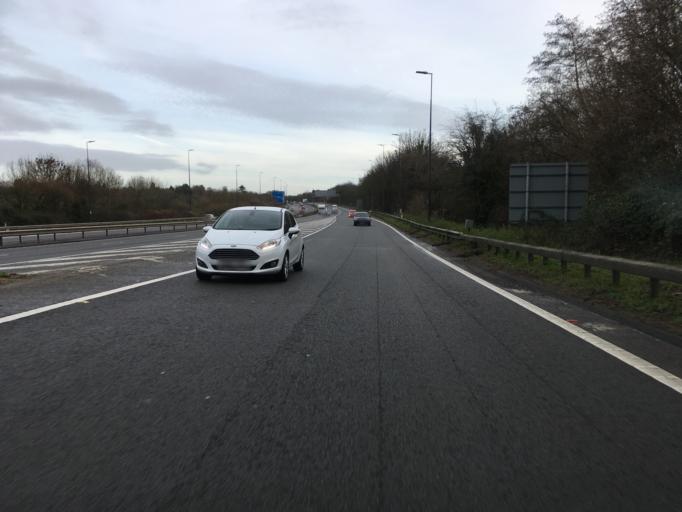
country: GB
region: Wales
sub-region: Monmouthshire
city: Magor
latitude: 51.5862
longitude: -2.8355
